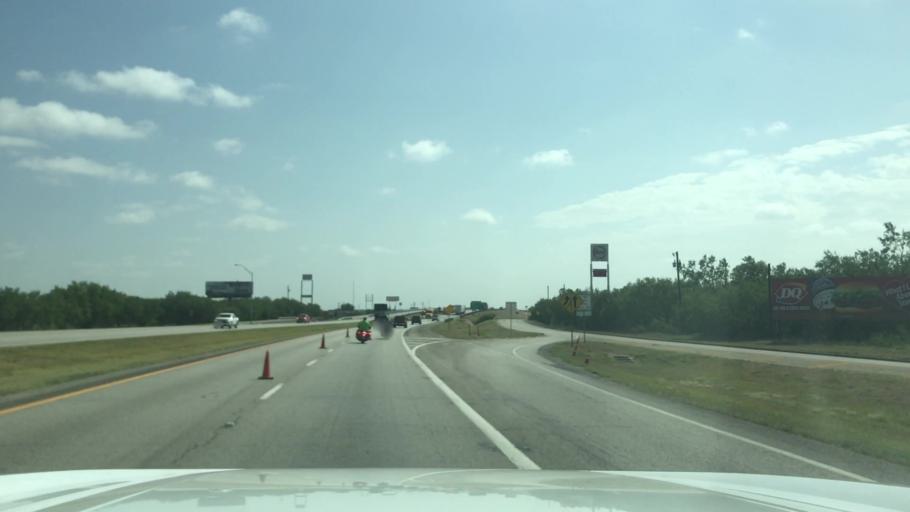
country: US
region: Texas
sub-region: Taylor County
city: Abilene
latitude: 32.4890
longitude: -99.7536
